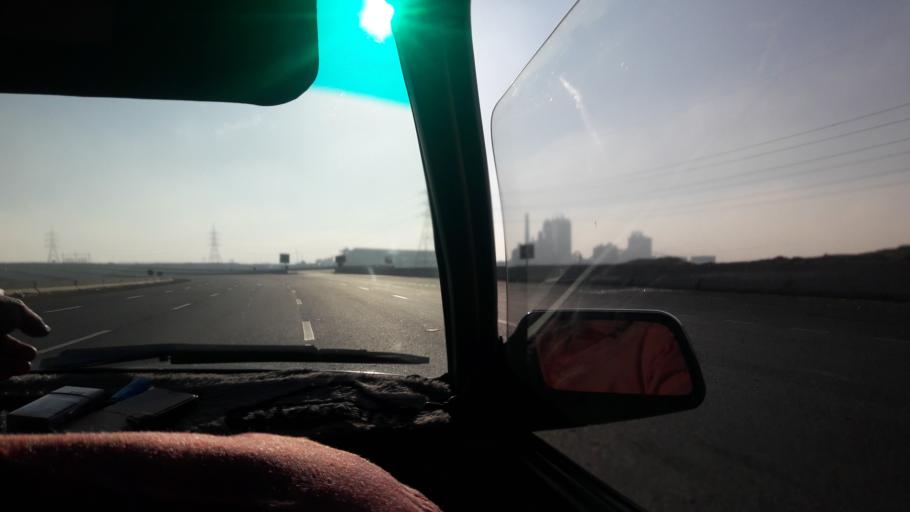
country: EG
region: Muhafazat al Qahirah
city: Halwan
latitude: 29.9188
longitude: 31.5169
